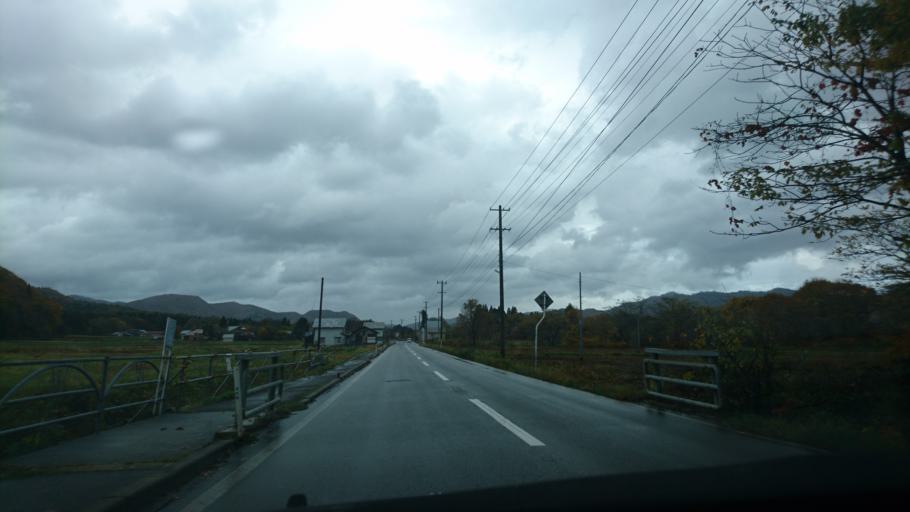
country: JP
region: Akita
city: Kakunodatemachi
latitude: 39.4550
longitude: 140.7693
